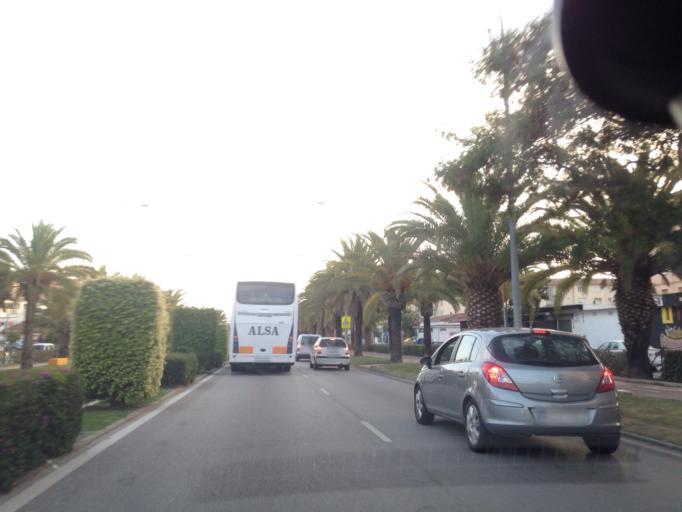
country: ES
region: Andalusia
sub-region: Provincia de Malaga
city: Malaga
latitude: 36.7442
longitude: -4.4229
